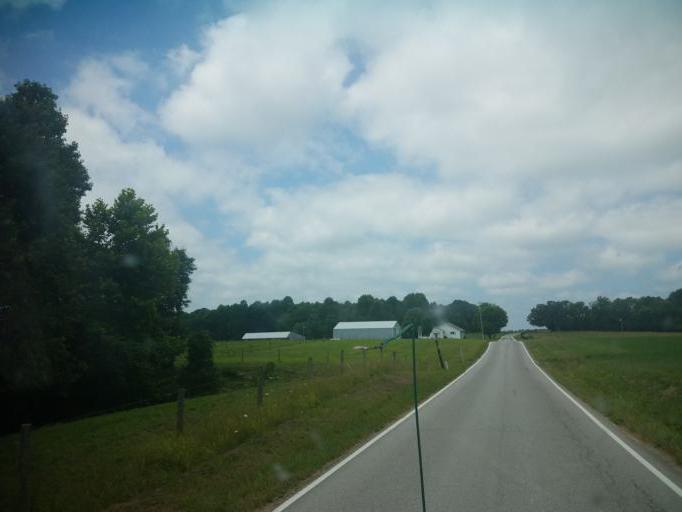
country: US
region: Kentucky
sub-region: Hart County
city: Munfordville
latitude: 37.3383
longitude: -86.0294
